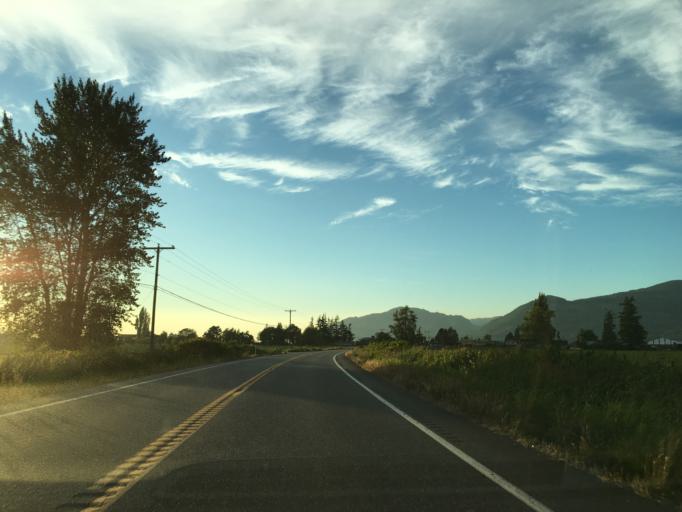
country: US
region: Washington
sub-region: Skagit County
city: Burlington
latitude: 48.5614
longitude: -122.4208
